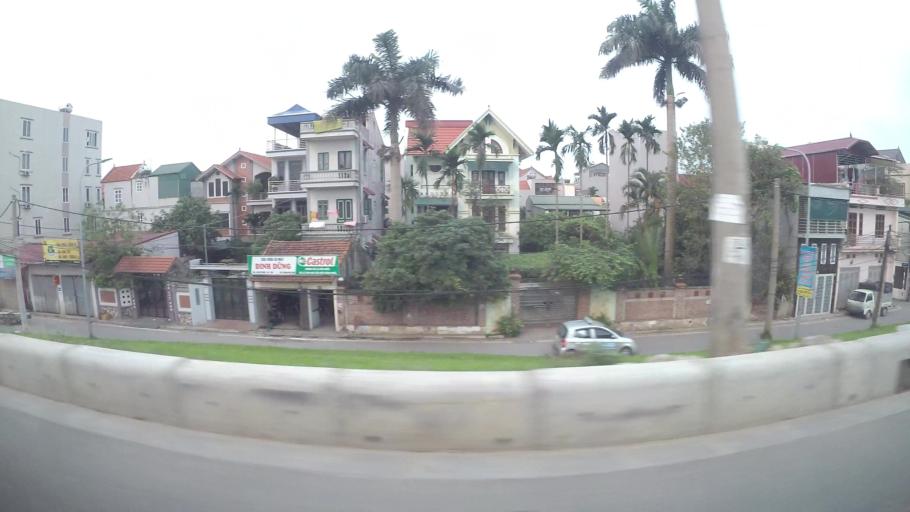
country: VN
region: Ha Noi
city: Hoan Kiem
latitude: 21.0266
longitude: 105.8831
